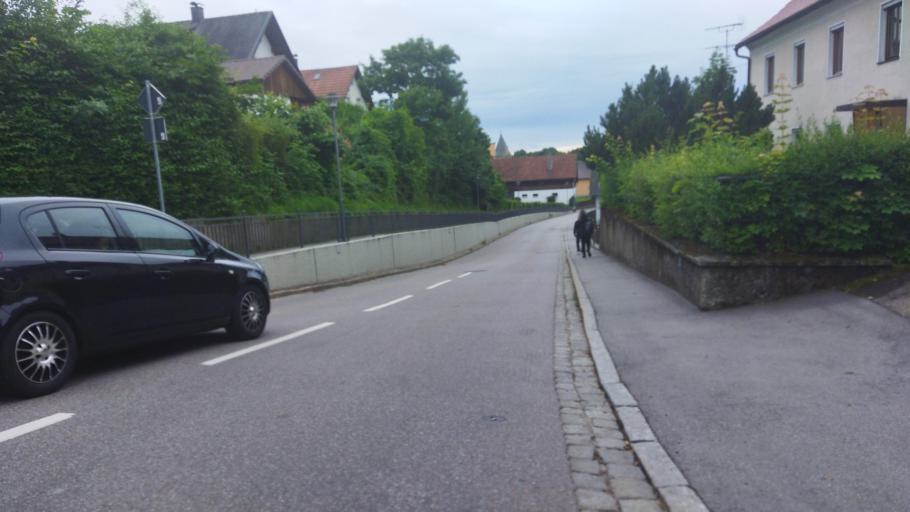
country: DE
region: Bavaria
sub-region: Upper Palatinate
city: Worth an der Donau
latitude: 49.0007
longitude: 12.4074
